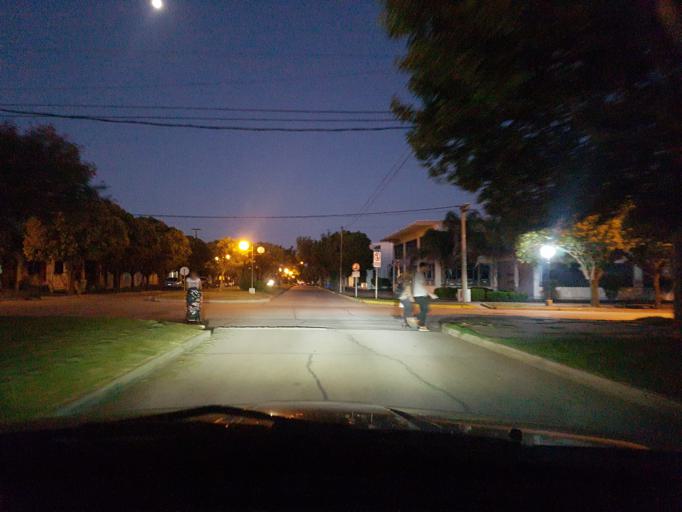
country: AR
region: Cordoba
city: General Cabrera
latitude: -32.7614
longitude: -63.7890
